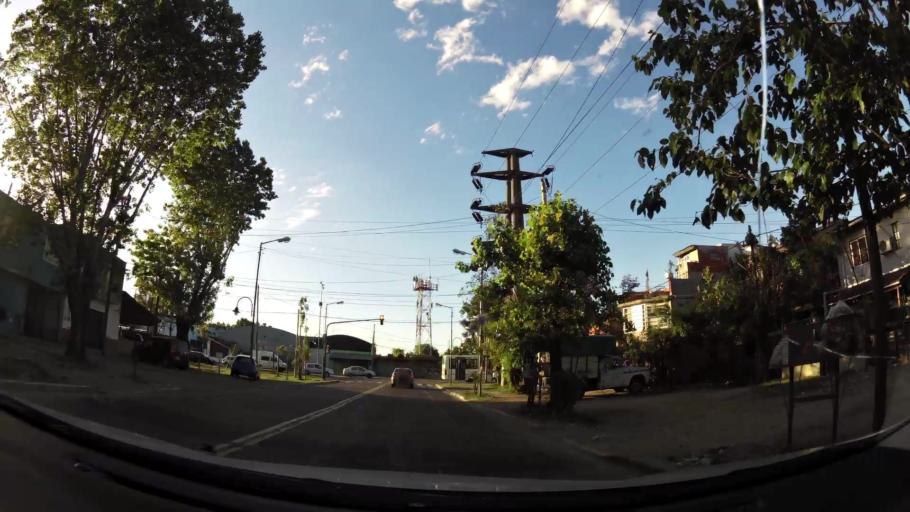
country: AR
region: Buenos Aires
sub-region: Partido de Tigre
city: Tigre
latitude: -34.4435
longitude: -58.5774
